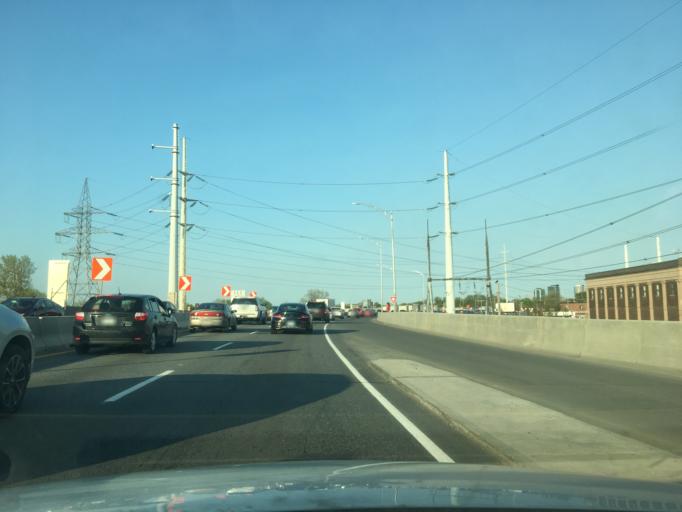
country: CA
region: Quebec
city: Westmount
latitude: 45.4744
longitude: -73.5735
